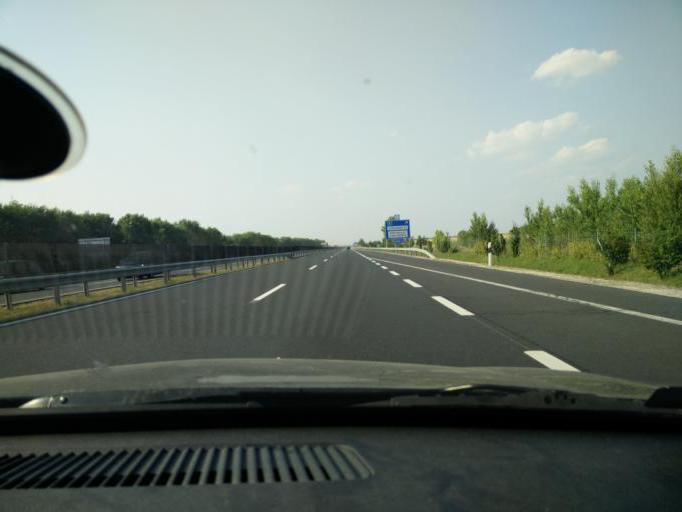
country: HU
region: Fejer
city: Rackeresztur
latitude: 47.2897
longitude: 18.8640
